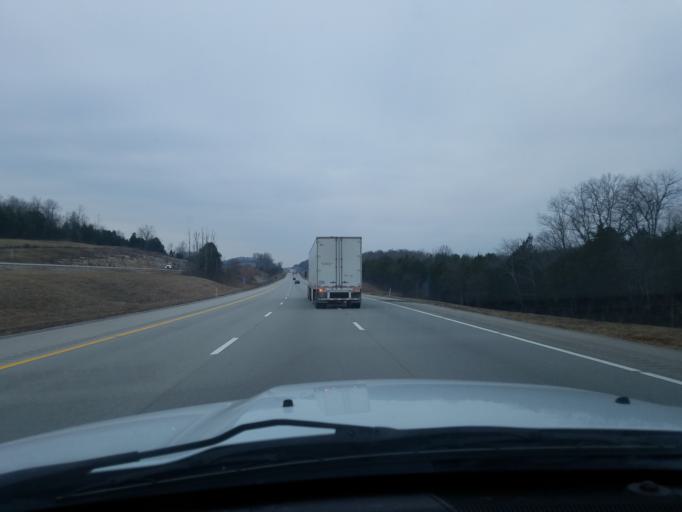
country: US
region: Kentucky
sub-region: Barren County
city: Cave City
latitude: 37.1193
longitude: -86.0167
